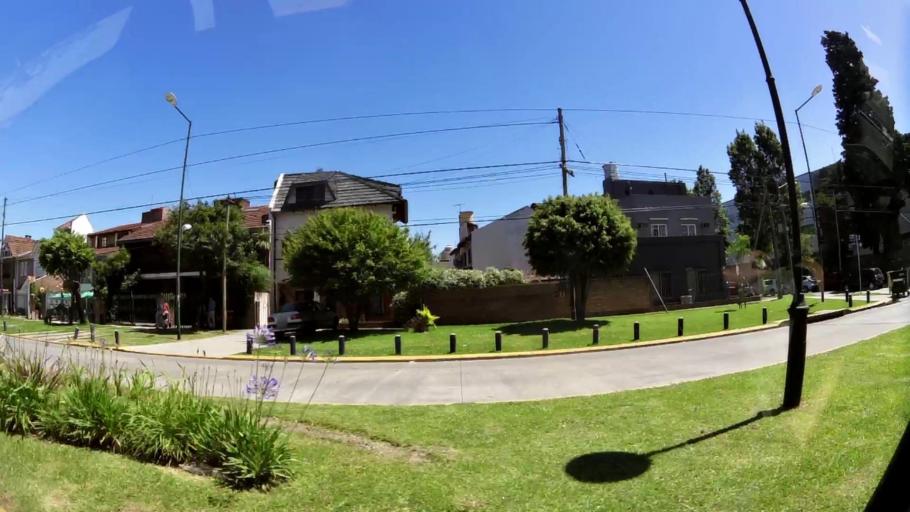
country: AR
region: Buenos Aires
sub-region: Partido de San Isidro
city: San Isidro
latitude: -34.4999
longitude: -58.5420
